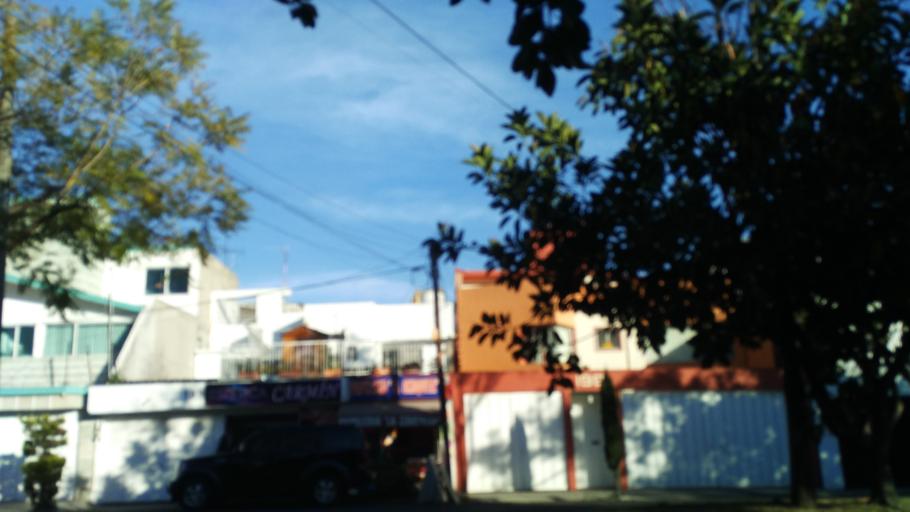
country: MX
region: Mexico City
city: Xochimilco
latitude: 19.2931
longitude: -99.1107
